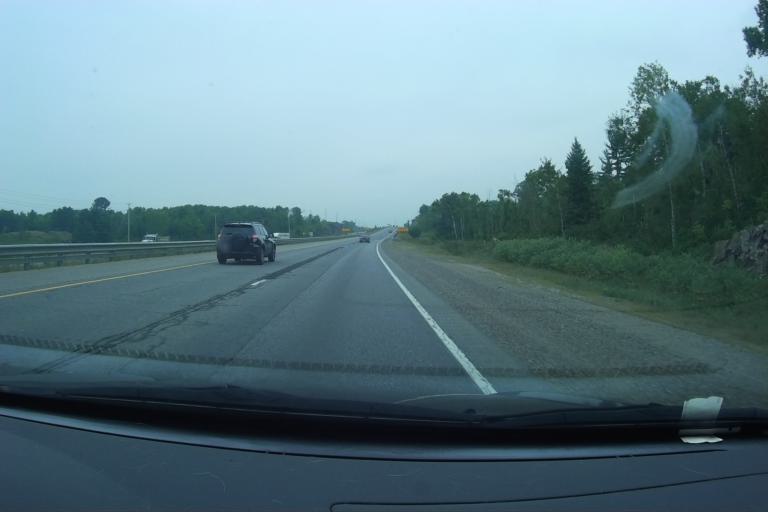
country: CA
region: Ontario
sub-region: Nipissing District
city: North Bay
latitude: 46.2906
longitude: -79.4196
